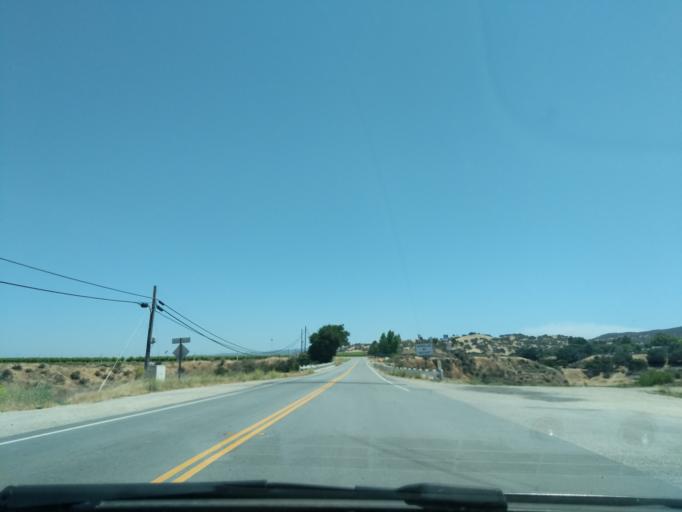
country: US
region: California
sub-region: Monterey County
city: King City
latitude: 36.1927
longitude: -121.1442
